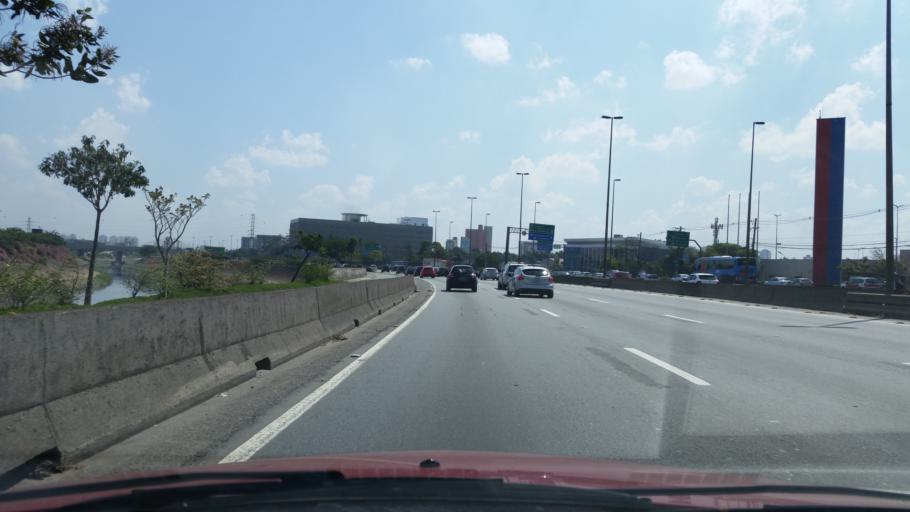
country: BR
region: Sao Paulo
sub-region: Sao Paulo
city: Sao Paulo
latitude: -23.5188
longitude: -46.6170
